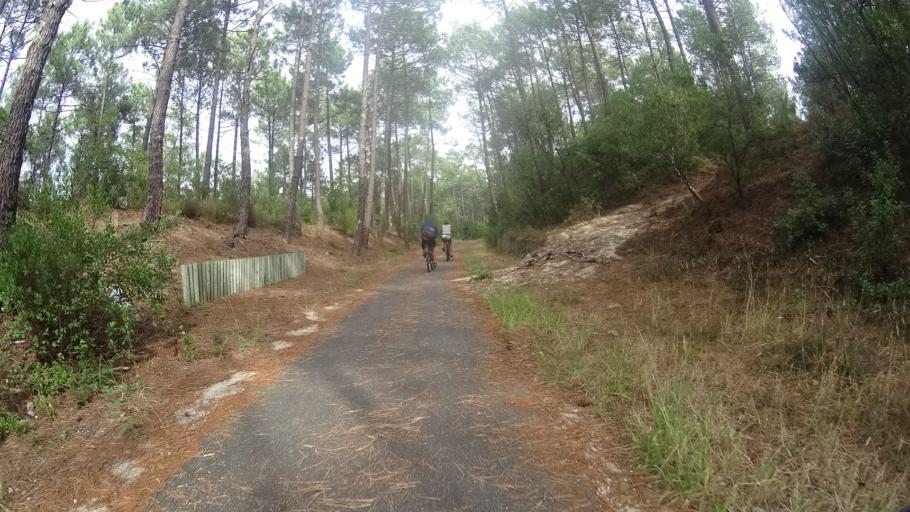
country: FR
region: Aquitaine
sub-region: Departement de la Gironde
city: Lacanau
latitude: 45.0075
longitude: -1.1475
